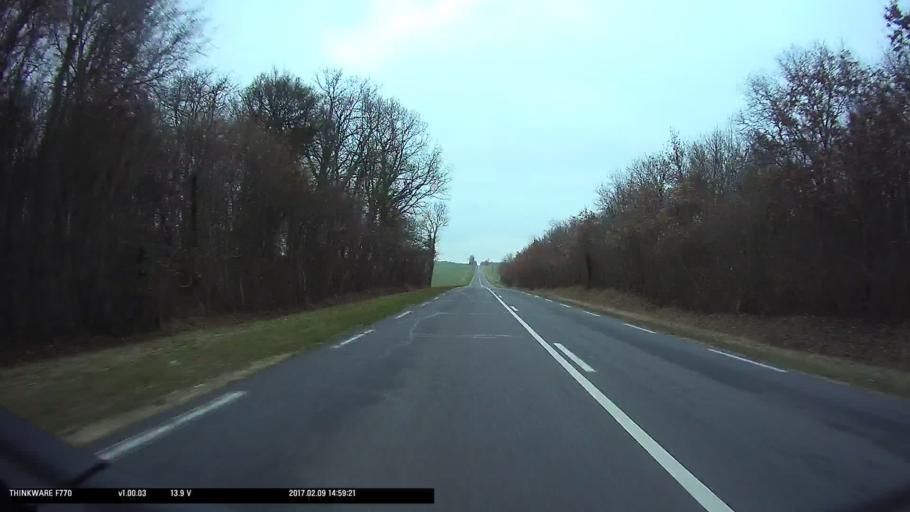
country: FR
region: Centre
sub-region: Departement du Cher
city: Levet
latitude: 46.8268
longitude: 2.4241
